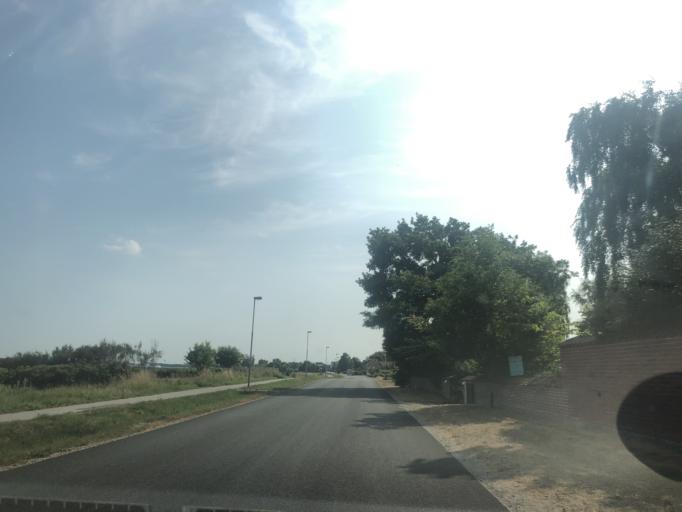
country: DK
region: North Denmark
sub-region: Morso Kommune
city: Nykobing Mors
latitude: 56.8112
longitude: 9.0217
